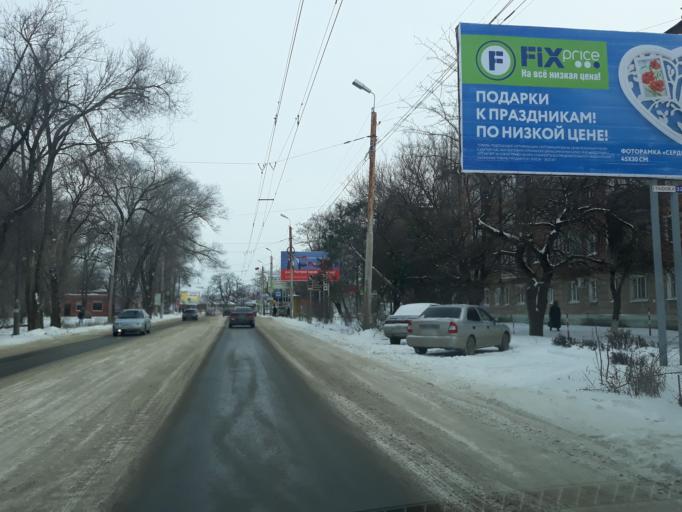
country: RU
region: Rostov
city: Taganrog
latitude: 47.2227
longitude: 38.8813
